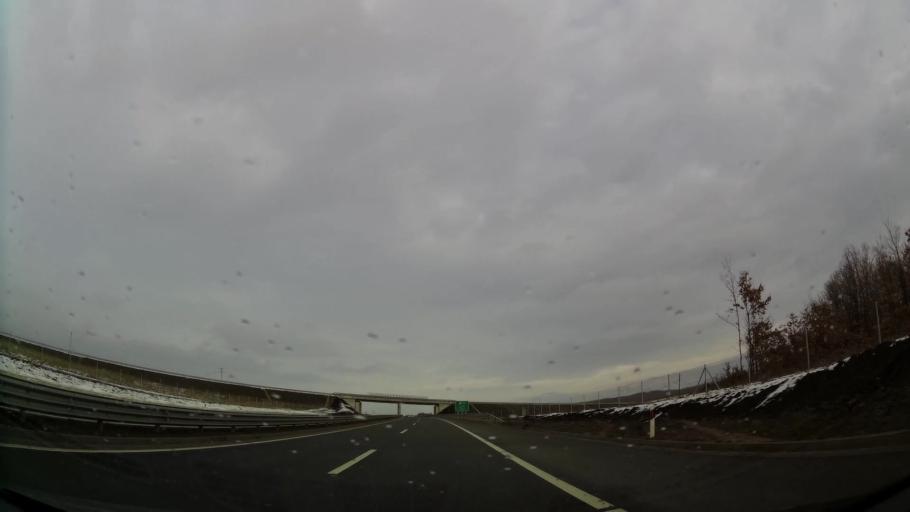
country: XK
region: Ferizaj
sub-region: Komuna e Ferizajt
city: Ferizaj
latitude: 42.3485
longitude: 21.2054
